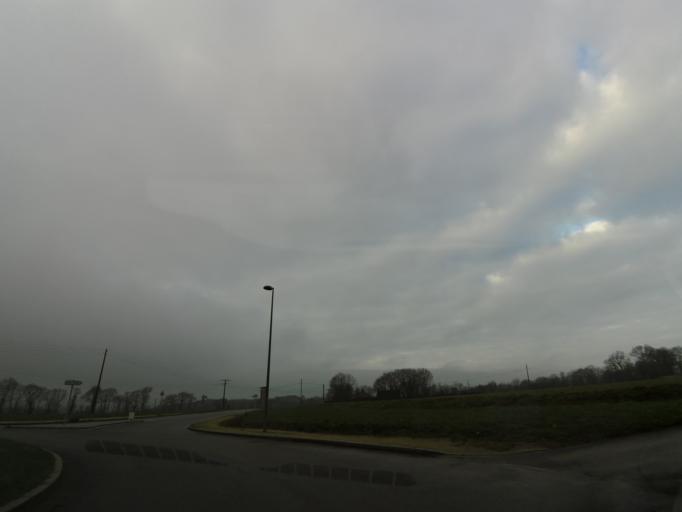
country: FR
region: Brittany
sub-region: Departement d'Ille-et-Vilaine
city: Laille
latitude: 47.9806
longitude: -1.7326
